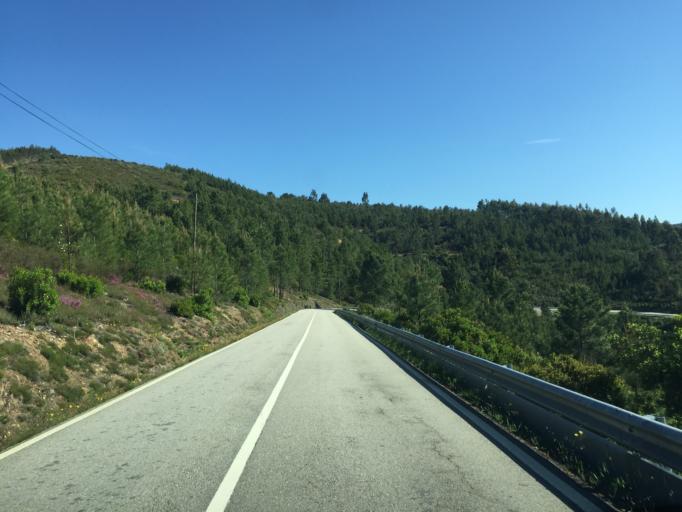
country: PT
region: Coimbra
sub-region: Pampilhosa da Serra
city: Pampilhosa da Serra
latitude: 40.0420
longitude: -7.8785
